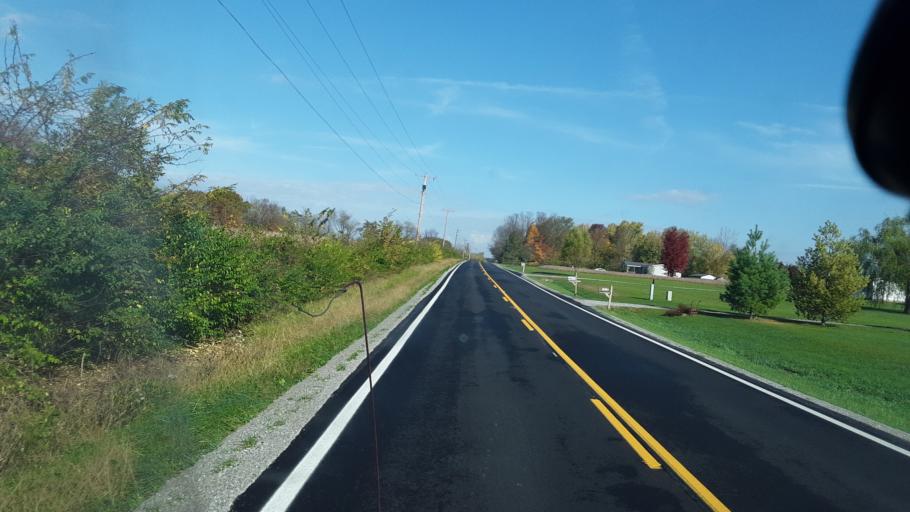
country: US
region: Ohio
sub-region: Highland County
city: Leesburg
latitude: 39.3719
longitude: -83.5934
